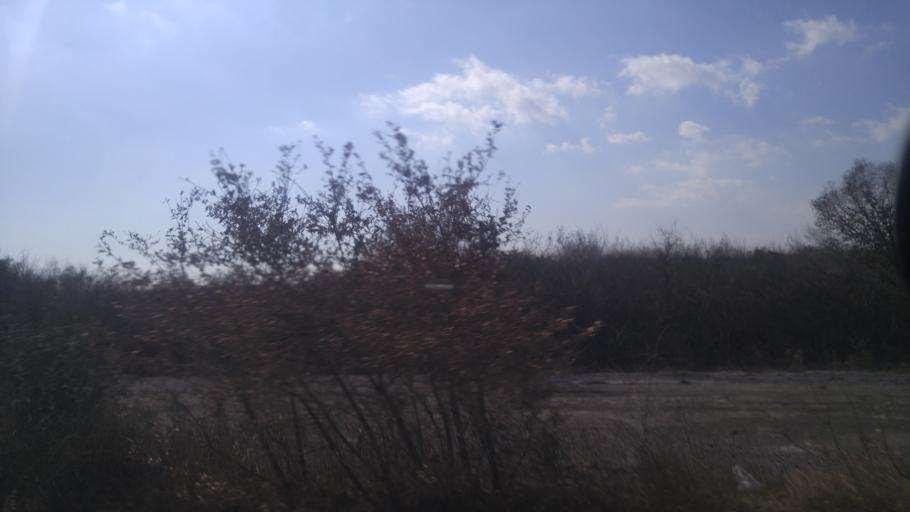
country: TR
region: Istanbul
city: Canta
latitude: 41.1670
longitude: 28.0991
